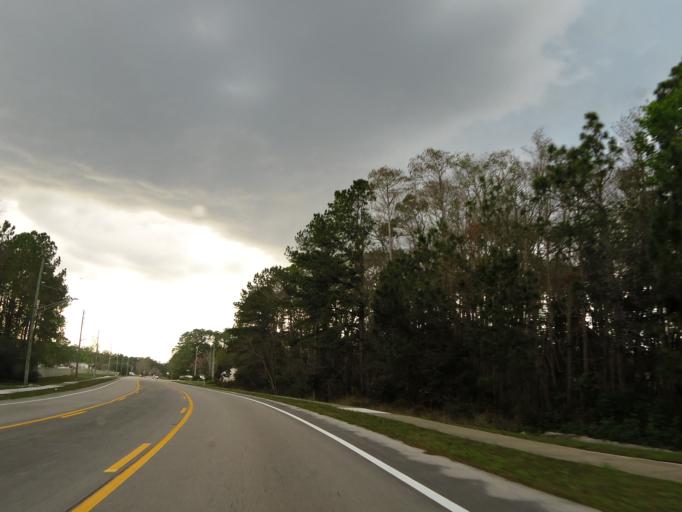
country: US
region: Florida
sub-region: Saint Johns County
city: Fruit Cove
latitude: 30.1814
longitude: -81.5692
